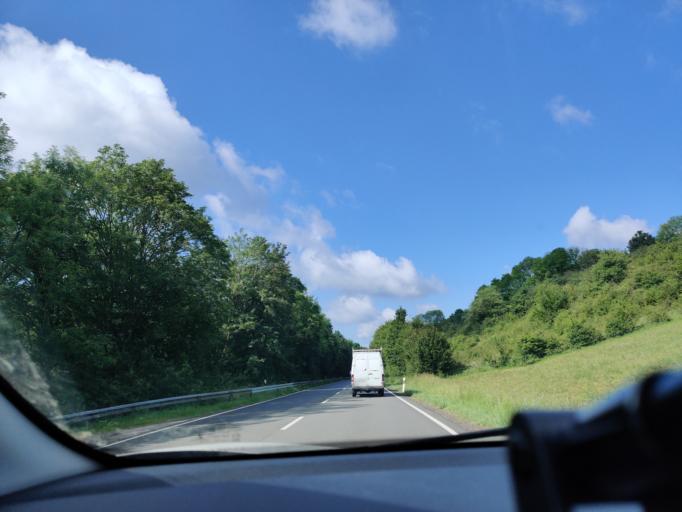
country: FR
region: Lorraine
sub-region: Departement de la Moselle
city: Bliesbruck
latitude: 49.1402
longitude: 7.1458
